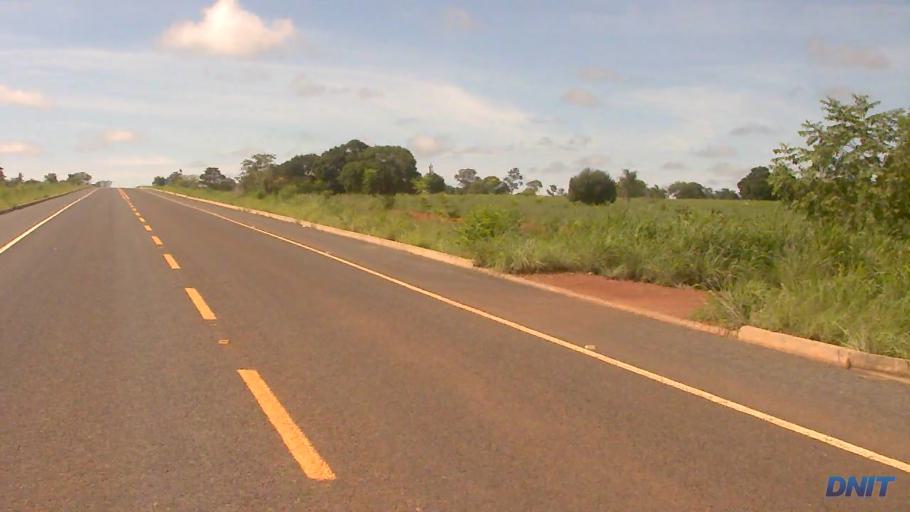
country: BR
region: Goias
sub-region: Sao Miguel Do Araguaia
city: Sao Miguel do Araguaia
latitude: -13.2989
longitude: -50.1756
